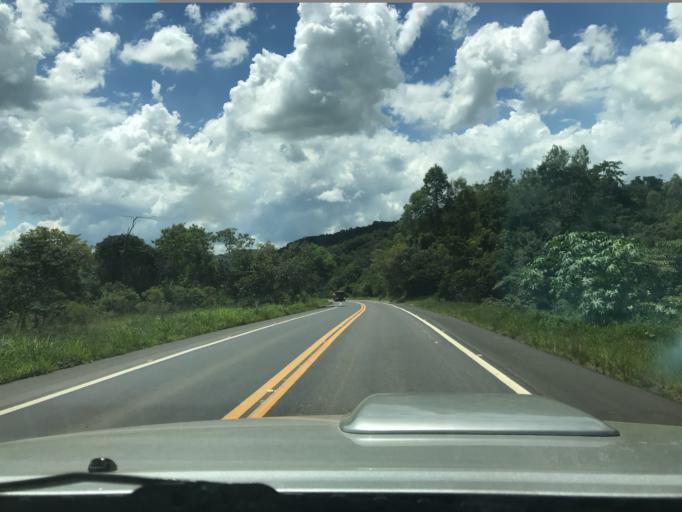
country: BR
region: Minas Gerais
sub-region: Formiga
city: Formiga
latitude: -20.6481
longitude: -45.3583
